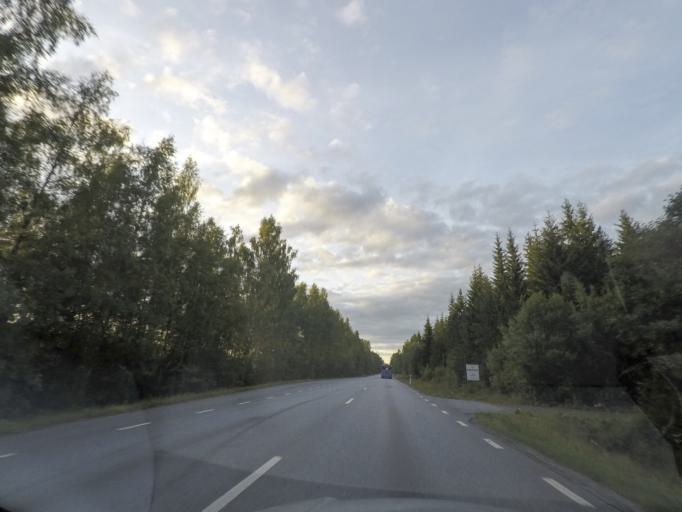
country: SE
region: OErebro
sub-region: Hallefors Kommun
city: Haellefors
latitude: 59.6852
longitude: 14.5510
